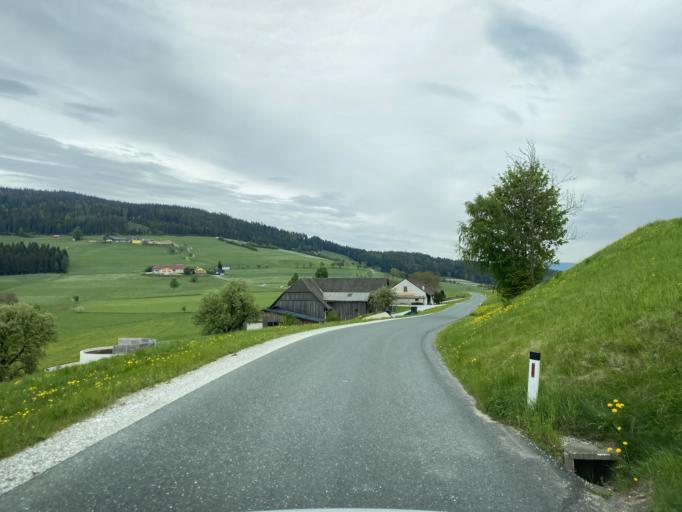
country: AT
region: Styria
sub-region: Politischer Bezirk Weiz
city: Gschaid bei Birkfeld
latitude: 47.3374
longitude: 15.7394
